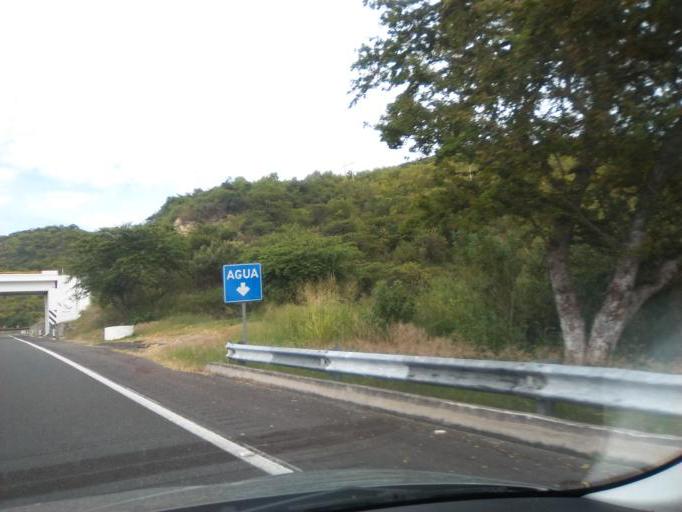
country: MX
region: Guerrero
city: Huitziltepec
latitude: 17.7099
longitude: -99.5094
